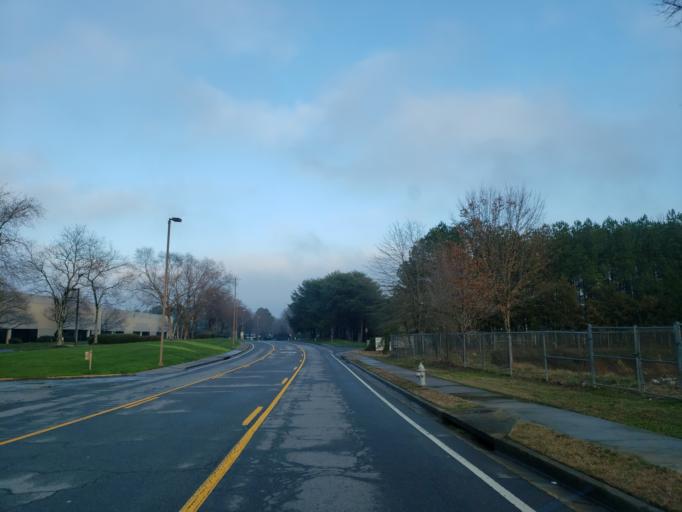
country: US
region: Georgia
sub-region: Cobb County
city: Kennesaw
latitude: 34.0105
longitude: -84.5984
